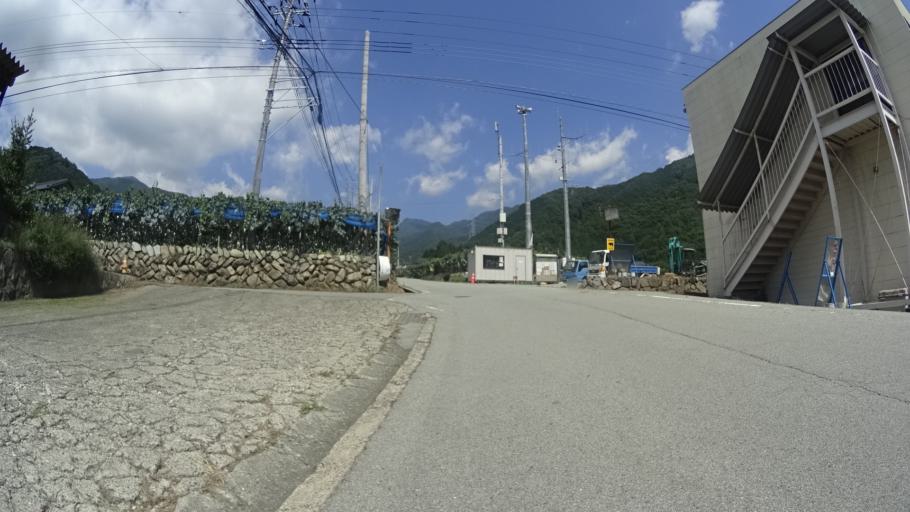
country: JP
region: Yamanashi
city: Enzan
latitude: 35.7684
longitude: 138.7035
